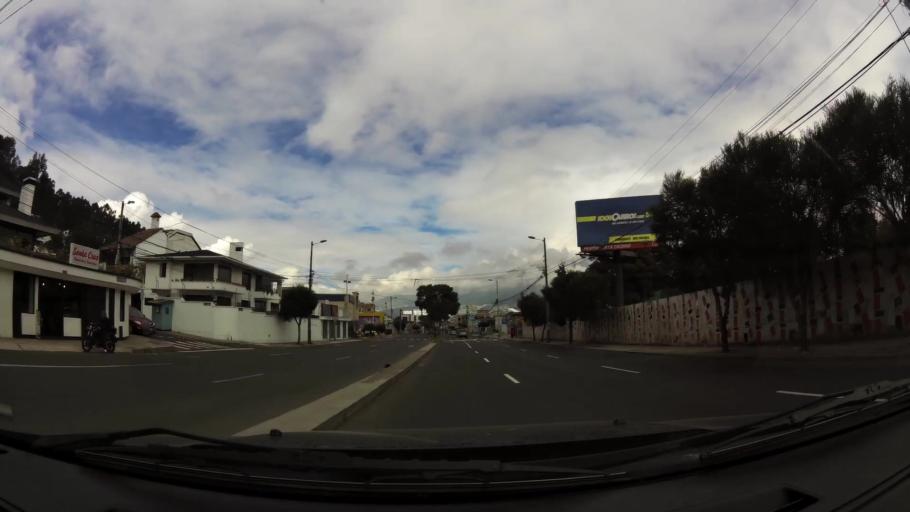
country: EC
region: Pichincha
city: Quito
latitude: -0.1638
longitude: -78.4643
